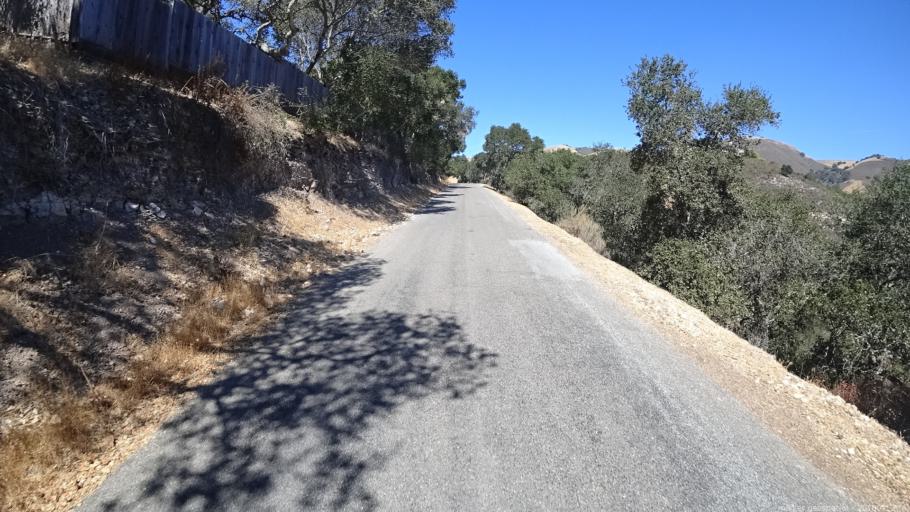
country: US
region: California
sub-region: Monterey County
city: Carmel Valley Village
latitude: 36.4851
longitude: -121.7210
